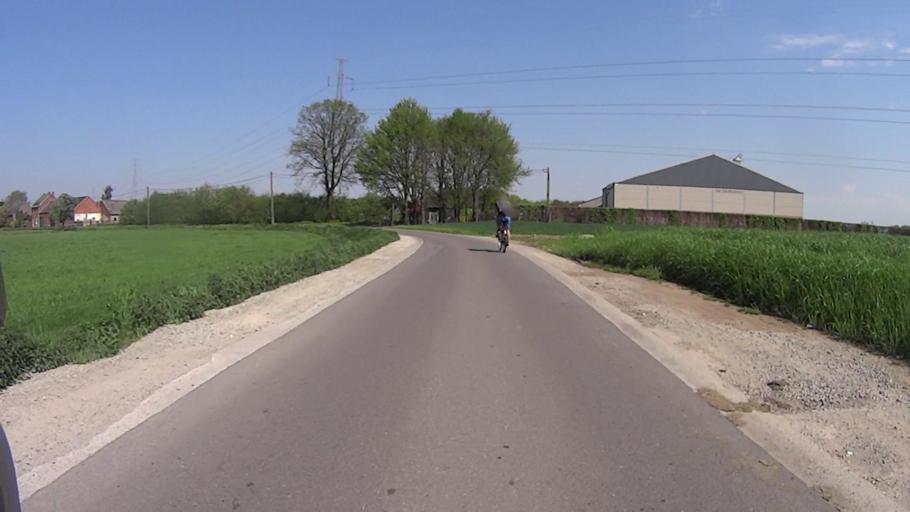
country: BE
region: Flanders
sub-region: Provincie Antwerpen
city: Sint-Amands
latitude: 51.0713
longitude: 4.2159
